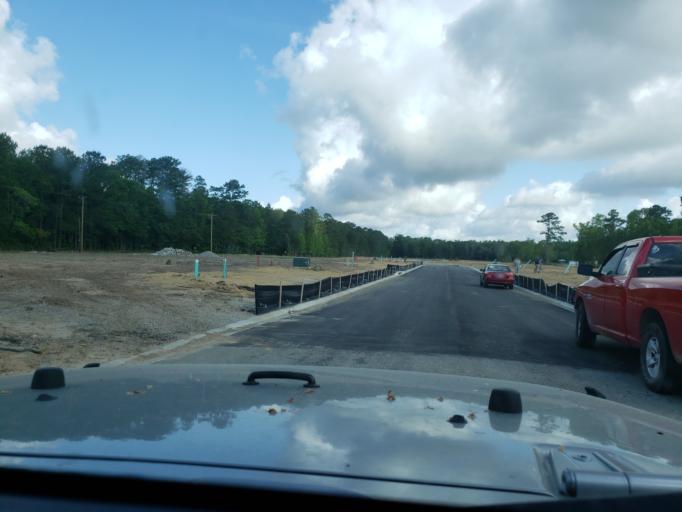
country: US
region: Georgia
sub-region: Chatham County
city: Georgetown
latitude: 32.0399
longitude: -81.2238
